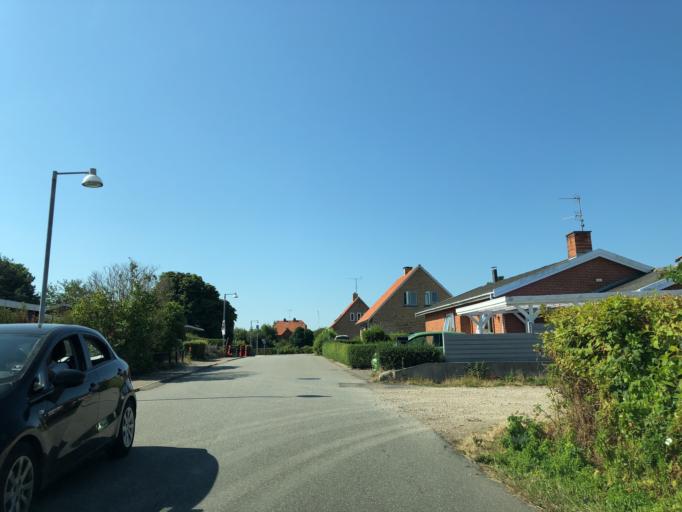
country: DK
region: Zealand
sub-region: Odsherred Kommune
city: Asnaes
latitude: 55.9693
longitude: 11.3648
